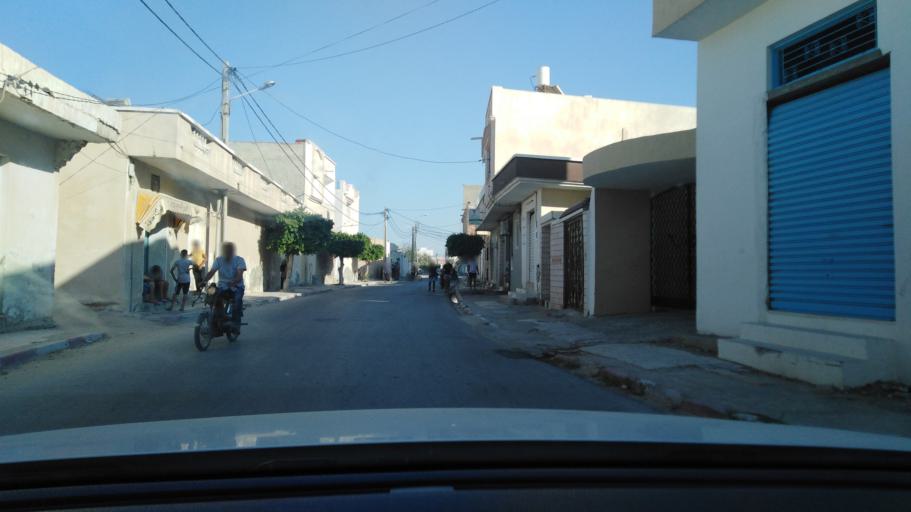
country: TN
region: Qabis
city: Gabes
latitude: 33.9368
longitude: 10.0689
